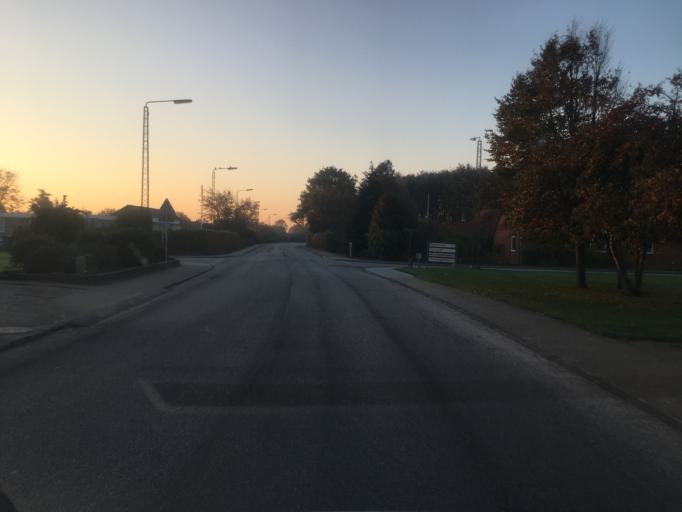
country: DK
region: South Denmark
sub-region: Tonder Kommune
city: Logumkloster
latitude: 55.0577
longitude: 8.9553
